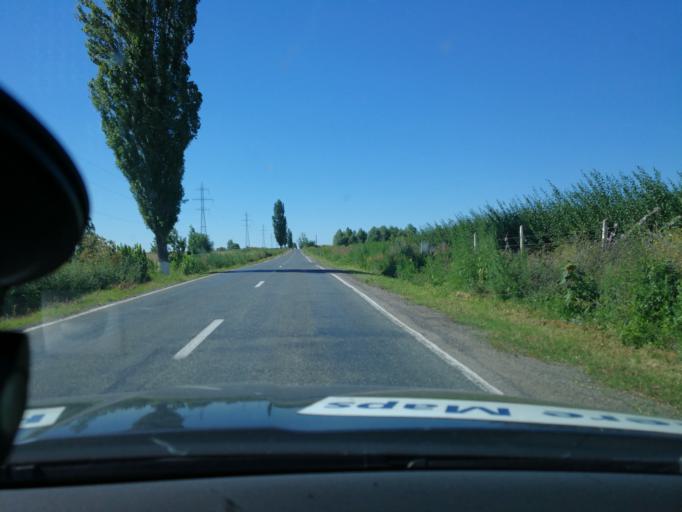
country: RO
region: Tulcea
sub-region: Comuna Greci
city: Greci
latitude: 45.1481
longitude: 28.2169
